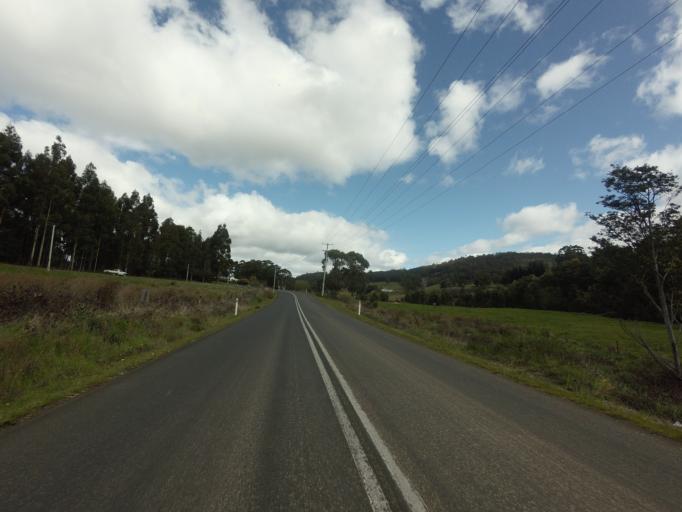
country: AU
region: Tasmania
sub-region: Huon Valley
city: Geeveston
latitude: -43.1767
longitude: 146.9239
